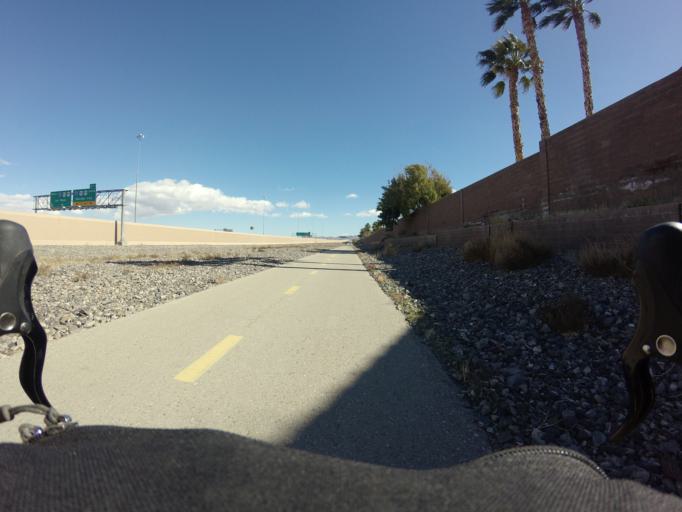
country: US
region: Nevada
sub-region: Clark County
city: Henderson
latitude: 36.0319
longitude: -115.0255
